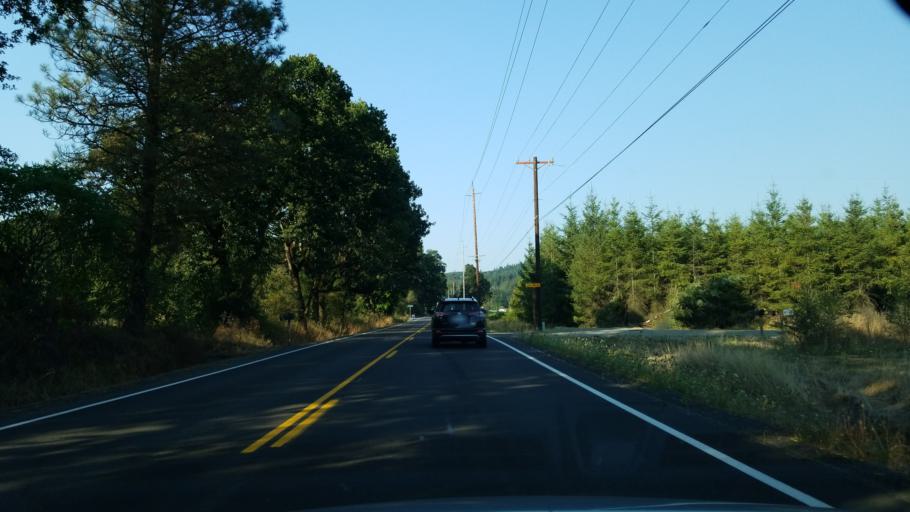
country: US
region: Oregon
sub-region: Clackamas County
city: Molalla
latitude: 45.1668
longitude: -122.5260
